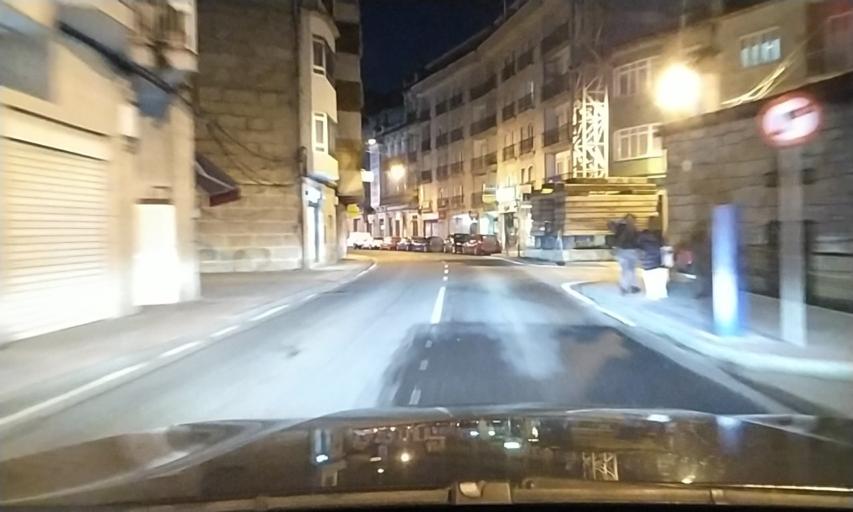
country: ES
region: Galicia
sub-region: Provincia de Ourense
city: Verin
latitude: 41.9403
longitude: -7.4401
